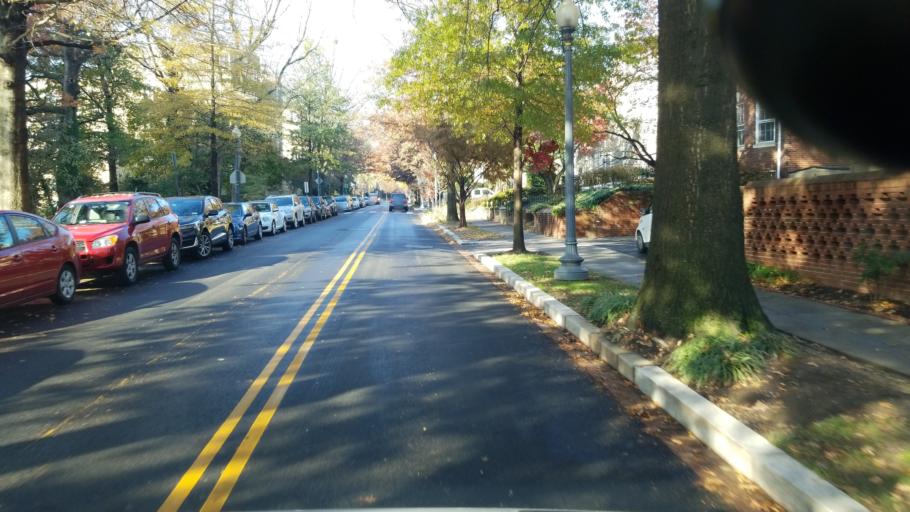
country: US
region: Washington, D.C.
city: Washington, D.C.
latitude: 38.9259
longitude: -77.0553
